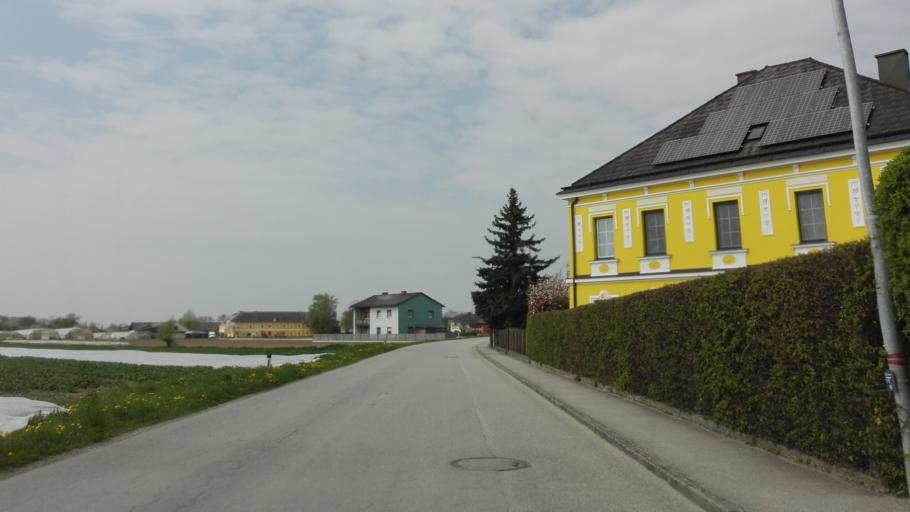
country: AT
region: Upper Austria
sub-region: Politischer Bezirk Perg
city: Perg
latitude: 48.2234
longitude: 14.6143
